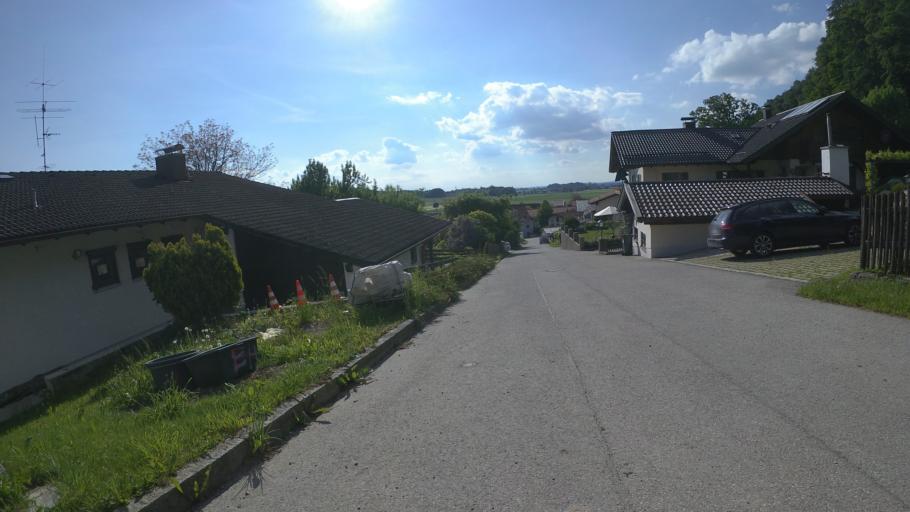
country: DE
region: Bavaria
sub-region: Upper Bavaria
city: Nussdorf
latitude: 47.8800
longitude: 12.5952
